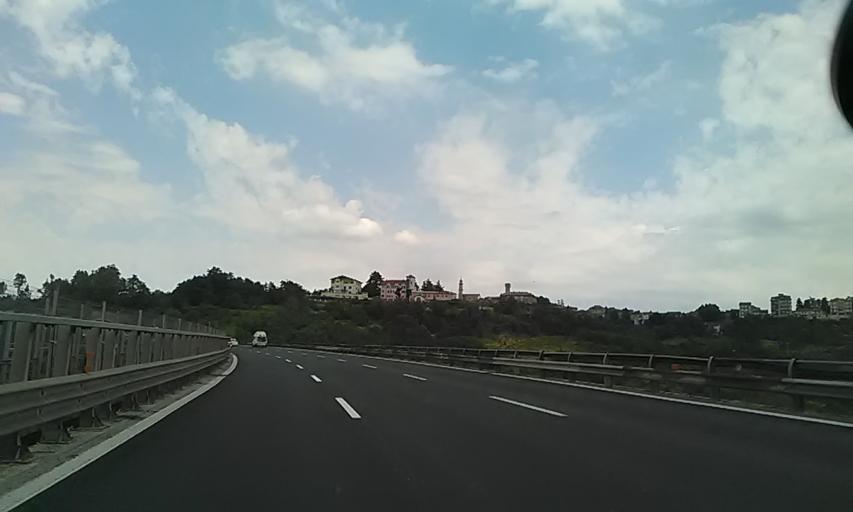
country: IT
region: Piedmont
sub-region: Provincia di Alessandria
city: Tagliolo Monferrato
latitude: 44.6326
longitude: 8.6626
